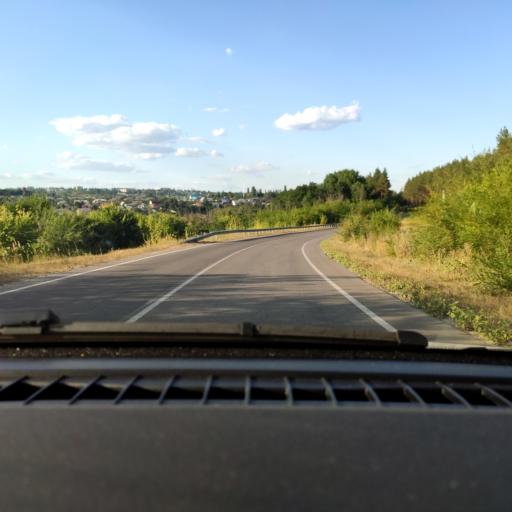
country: RU
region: Voronezj
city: Semiluki
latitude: 51.6686
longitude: 39.0213
